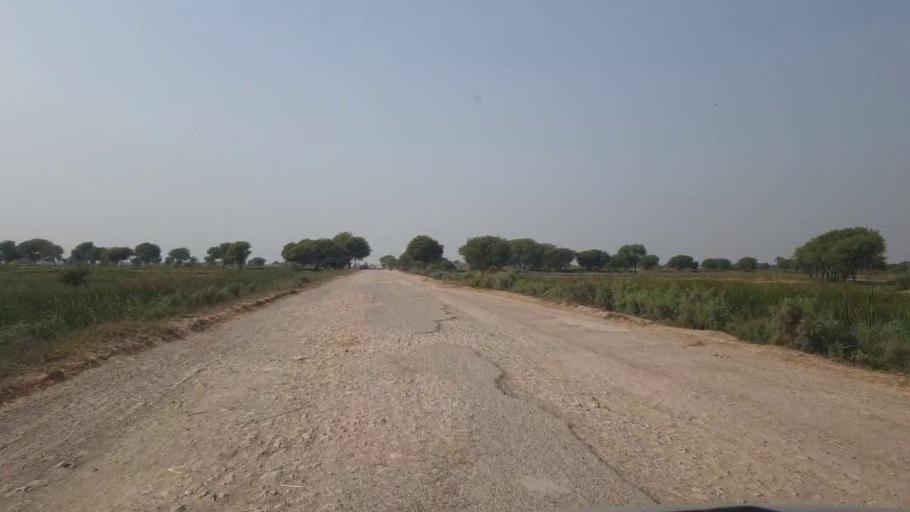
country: PK
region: Sindh
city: Matli
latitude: 25.0221
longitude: 68.6818
